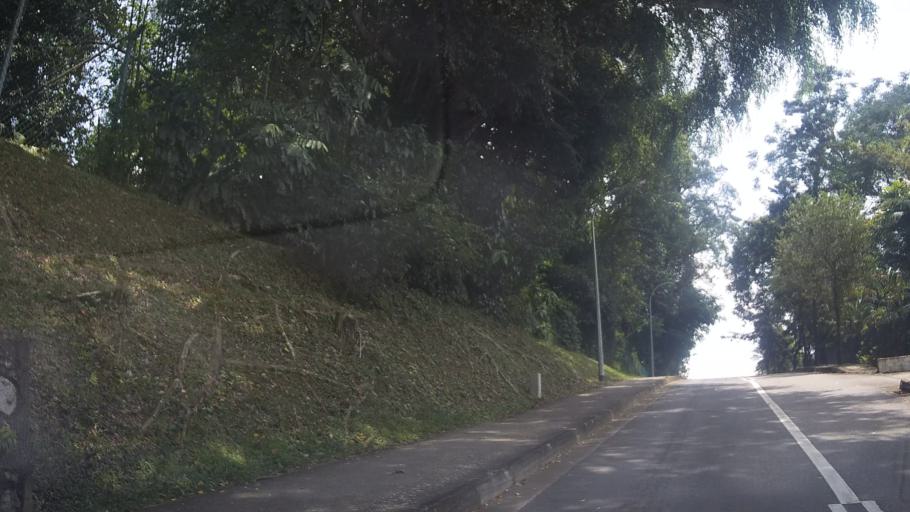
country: SG
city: Singapore
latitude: 1.3137
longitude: 103.7898
